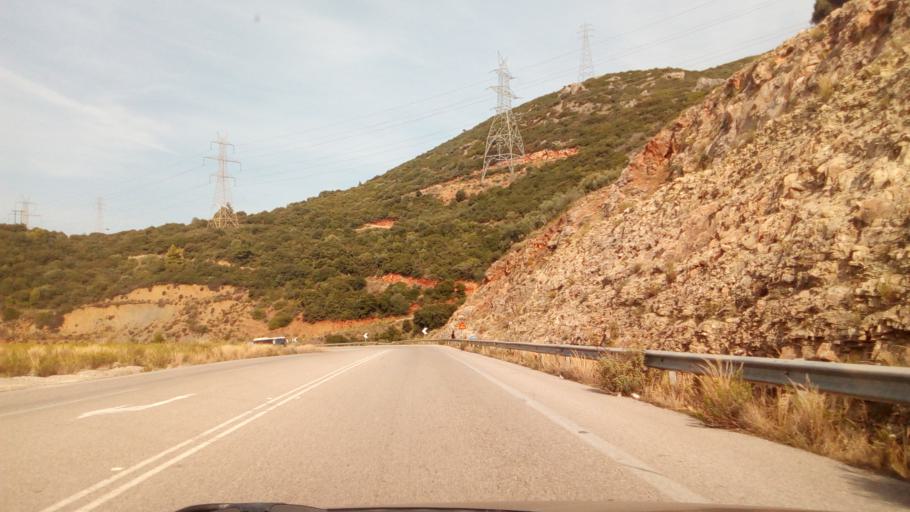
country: GR
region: West Greece
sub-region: Nomos Aitolias kai Akarnanias
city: Nafpaktos
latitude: 38.4002
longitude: 21.8215
